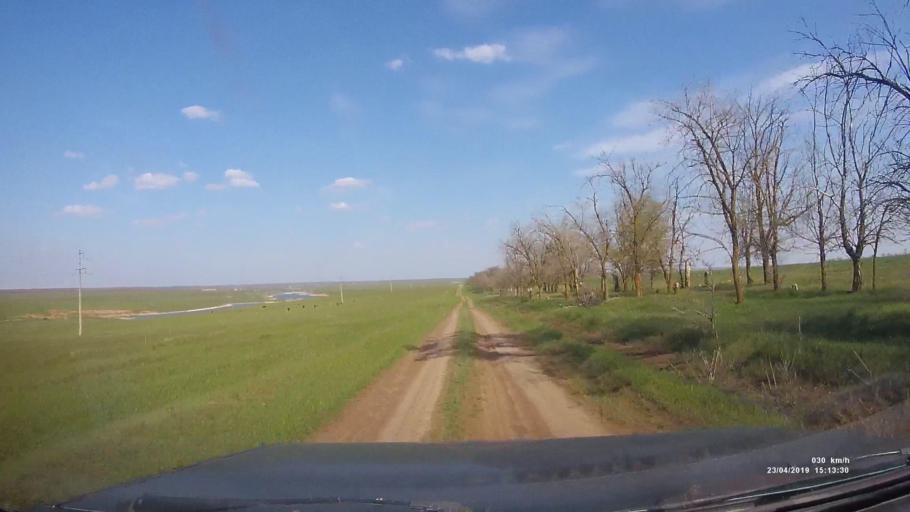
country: RU
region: Rostov
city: Remontnoye
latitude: 46.5397
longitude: 42.9564
